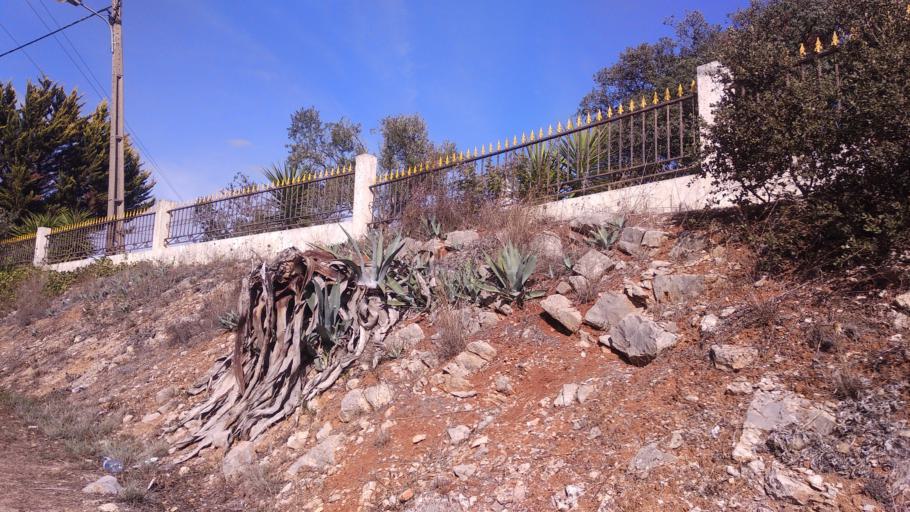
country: PT
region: Faro
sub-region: Sao Bras de Alportel
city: Sao Bras de Alportel
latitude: 37.1615
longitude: -7.8998
